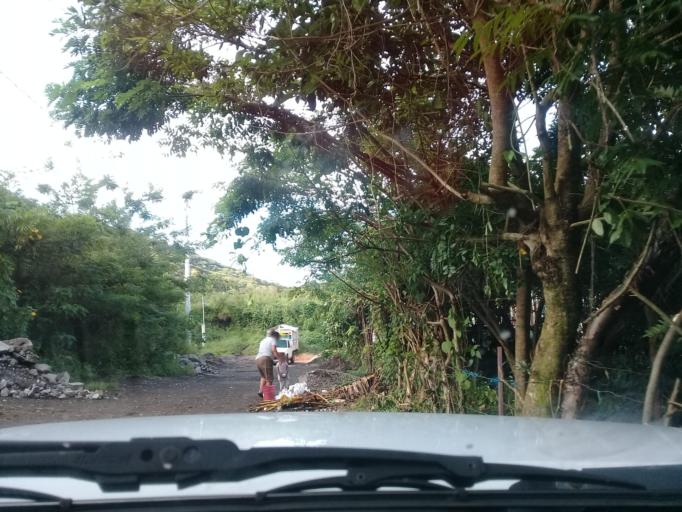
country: MX
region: Veracruz
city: Catemaco
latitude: 18.4352
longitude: -95.1089
